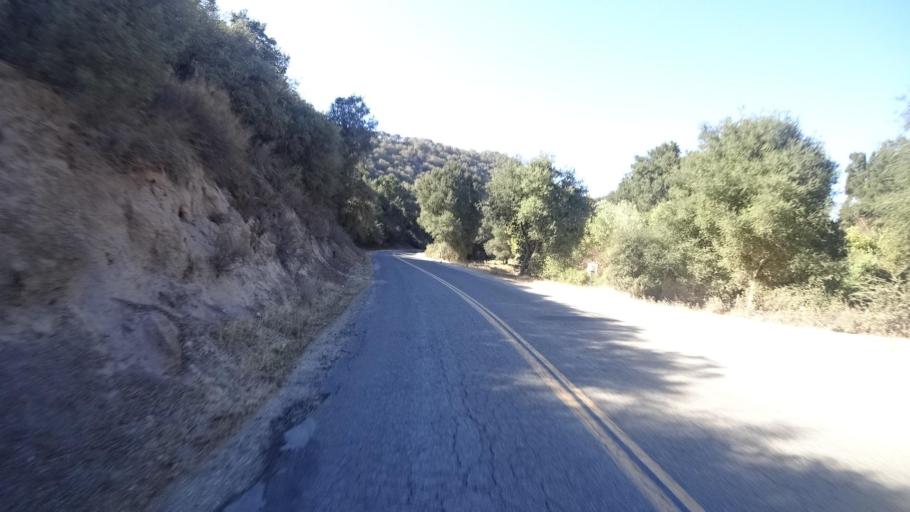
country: US
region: California
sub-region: Monterey County
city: King City
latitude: 36.1486
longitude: -121.1958
